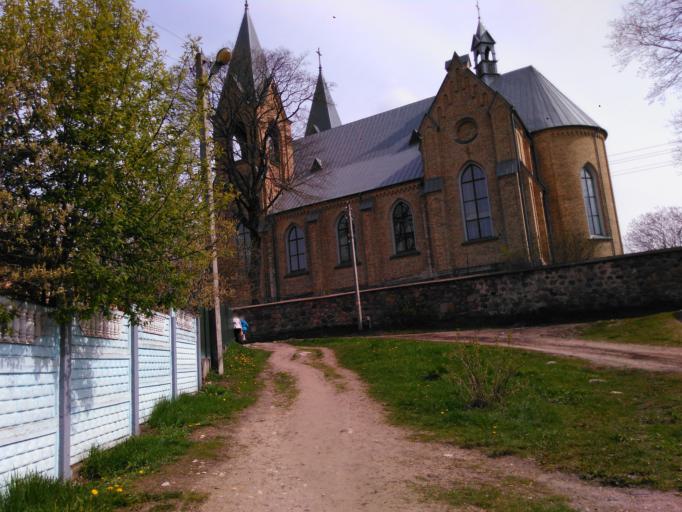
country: BY
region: Minsk
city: Rakaw
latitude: 53.9652
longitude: 27.0551
